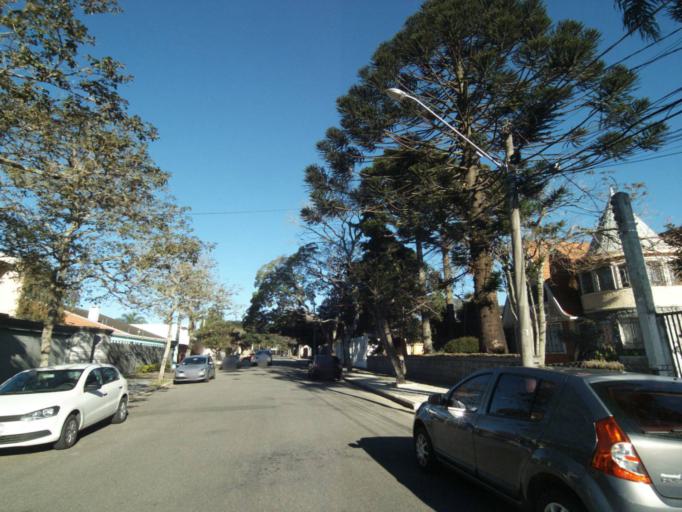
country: BR
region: Parana
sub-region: Curitiba
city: Curitiba
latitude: -25.4199
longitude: -49.2327
